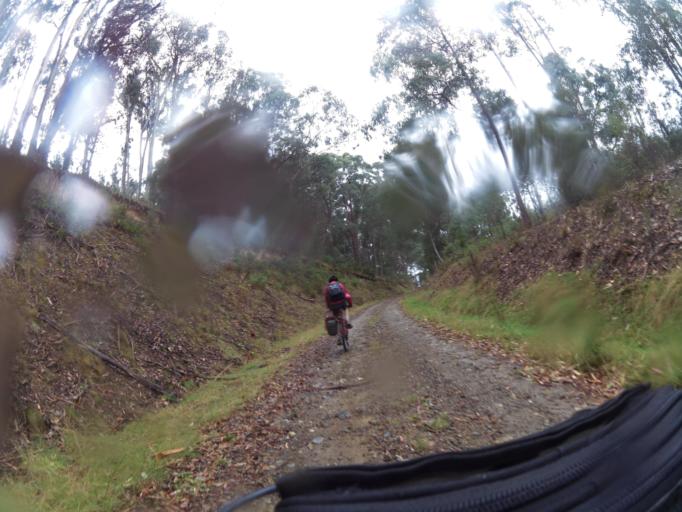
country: AU
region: New South Wales
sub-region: Greater Hume Shire
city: Holbrook
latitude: -36.2199
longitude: 147.5626
